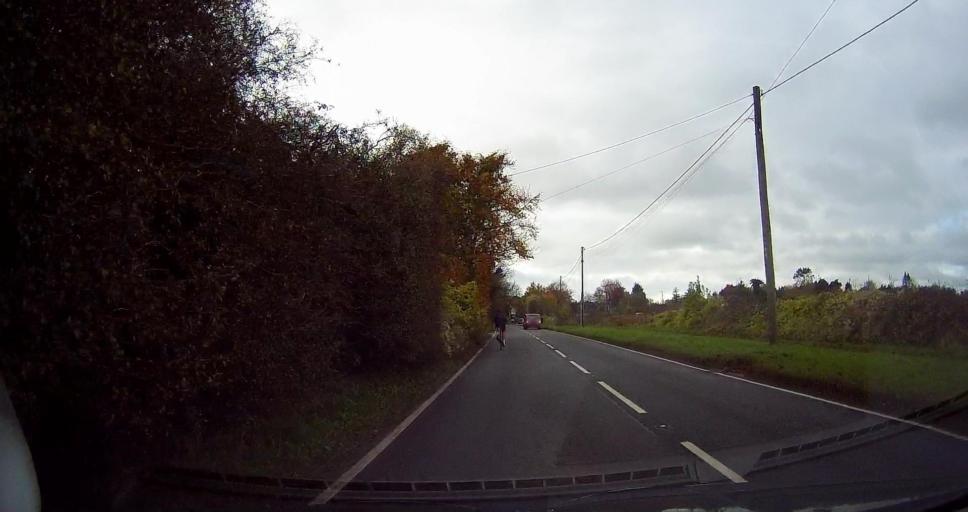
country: GB
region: England
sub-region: Kent
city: Meopham
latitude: 51.3499
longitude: 0.3498
